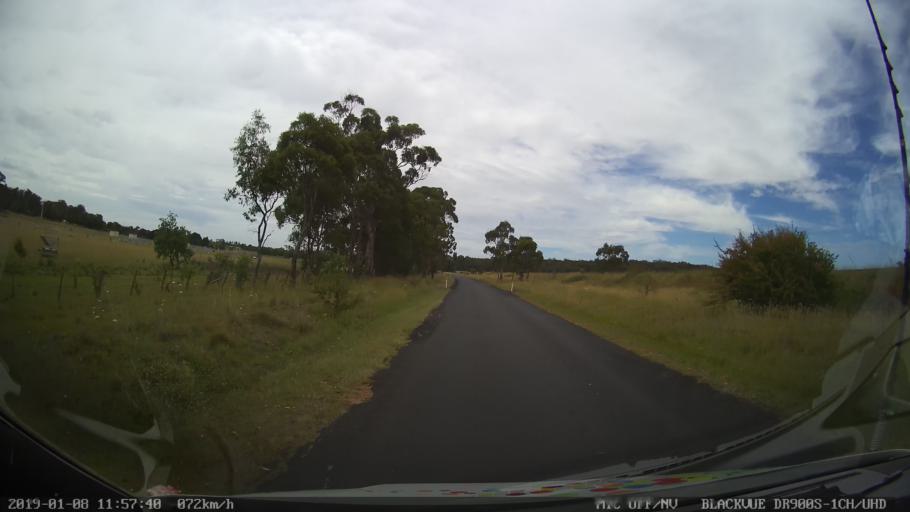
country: AU
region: New South Wales
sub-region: Armidale Dumaresq
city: Armidale
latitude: -30.4520
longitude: 151.5685
